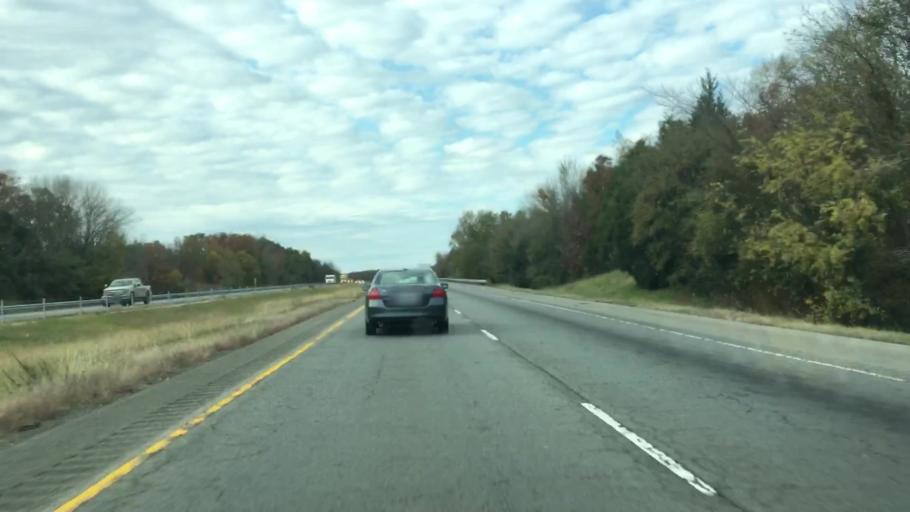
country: US
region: Arkansas
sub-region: Faulkner County
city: Conway
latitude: 35.1324
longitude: -92.5164
